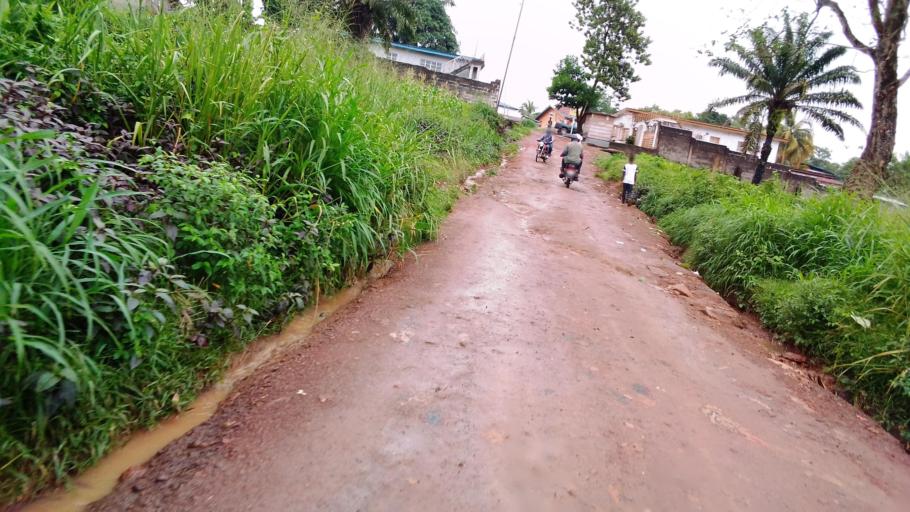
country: SL
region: Eastern Province
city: Kenema
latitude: 7.8956
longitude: -11.1807
